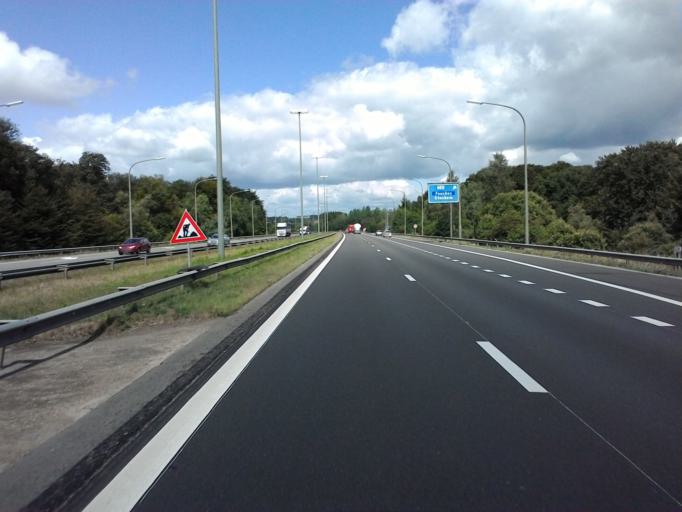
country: BE
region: Wallonia
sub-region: Province du Luxembourg
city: Arlon
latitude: 49.6833
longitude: 5.7540
